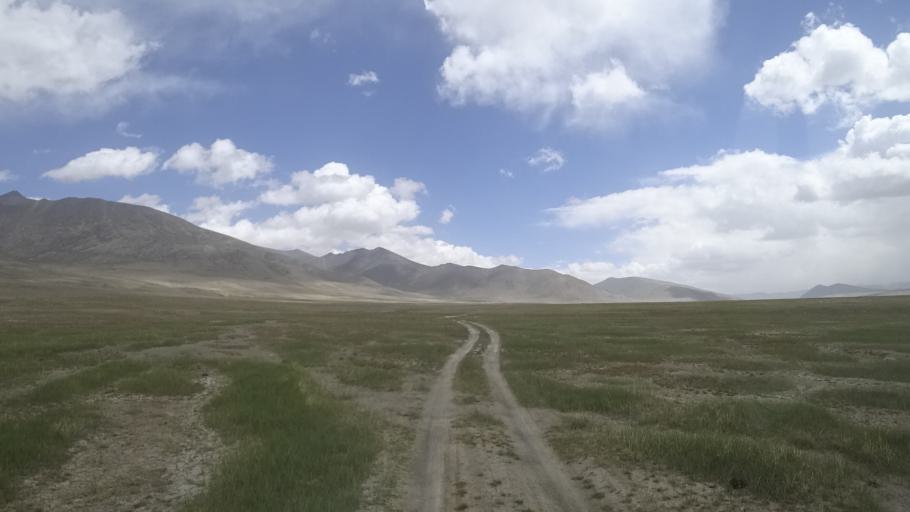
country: TJ
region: Gorno-Badakhshan
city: Murghob
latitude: 37.4831
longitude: 73.9836
